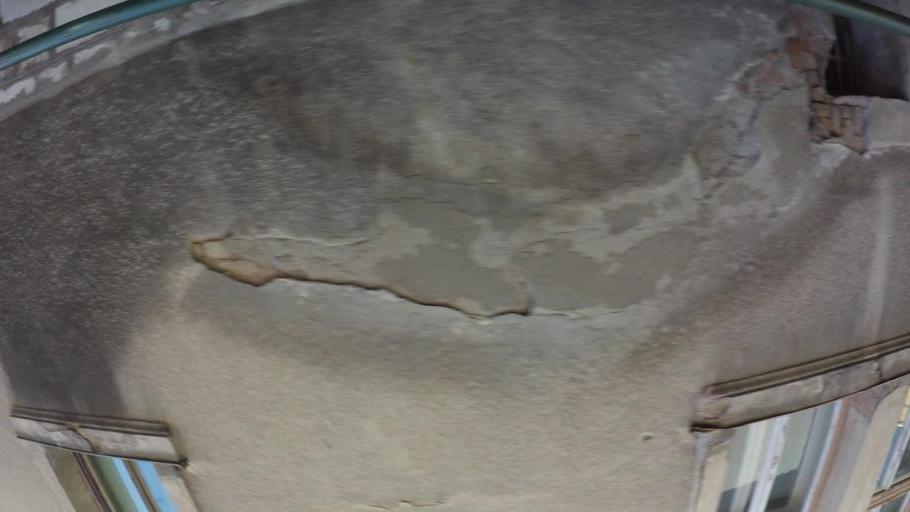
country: BA
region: Federation of Bosnia and Herzegovina
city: Kobilja Glava
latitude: 43.8622
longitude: 18.4209
